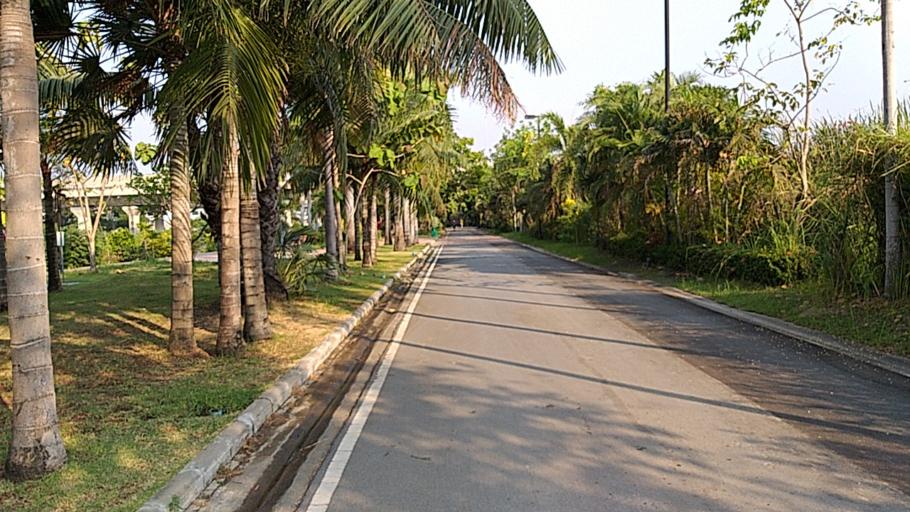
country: TH
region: Bangkok
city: Don Mueang
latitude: 13.9288
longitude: 100.5532
